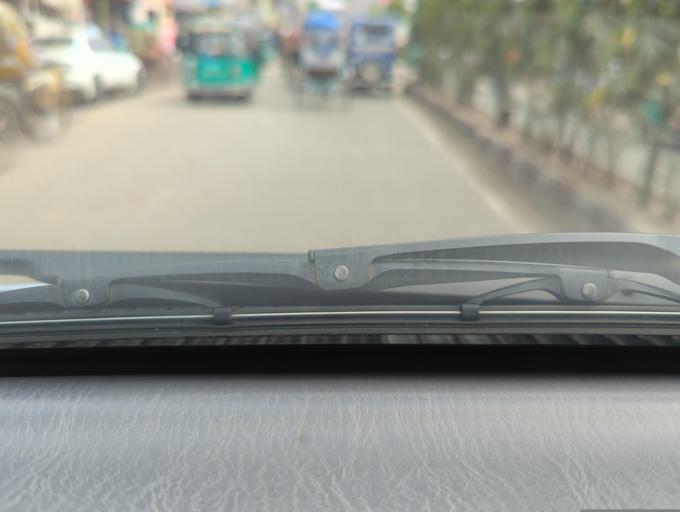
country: BD
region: Sylhet
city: Maulavi Bazar
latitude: 24.4898
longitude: 91.7605
